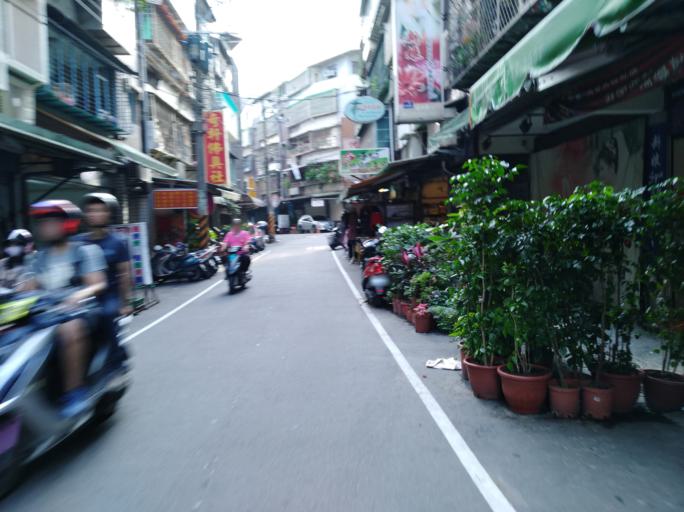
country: TW
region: Taipei
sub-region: Taipei
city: Banqiao
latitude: 25.0438
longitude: 121.4259
